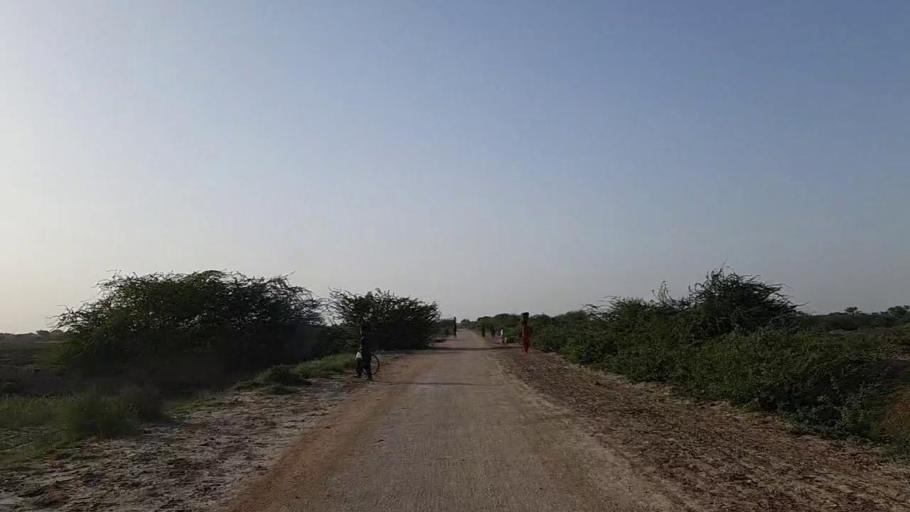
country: PK
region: Sindh
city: Jati
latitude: 24.3314
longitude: 68.1579
